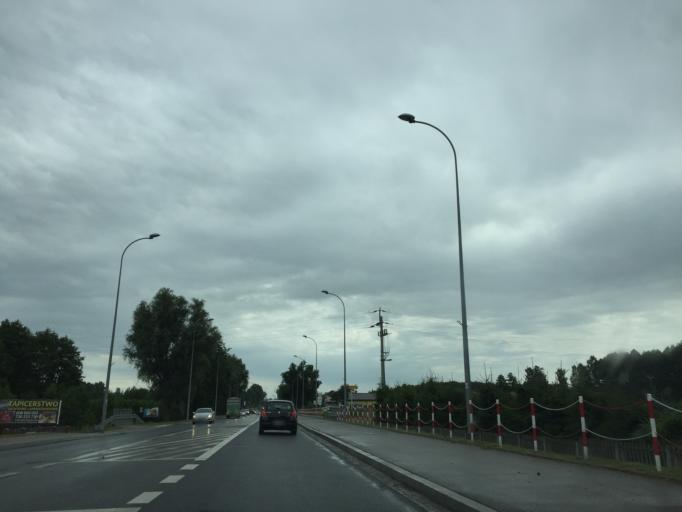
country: PL
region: Podlasie
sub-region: Bialystok
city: Bialystok
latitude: 53.0997
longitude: 23.2275
